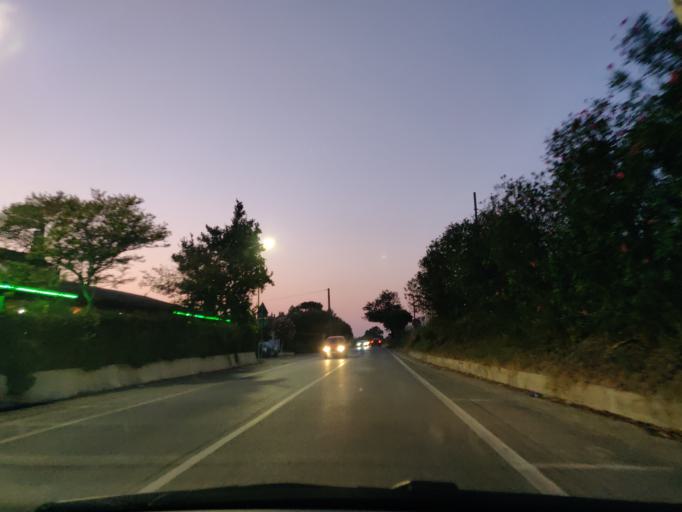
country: IT
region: Latium
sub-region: Citta metropolitana di Roma Capitale
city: Npp 23 (Parco Leonardo)
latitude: 41.8326
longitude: 12.2851
